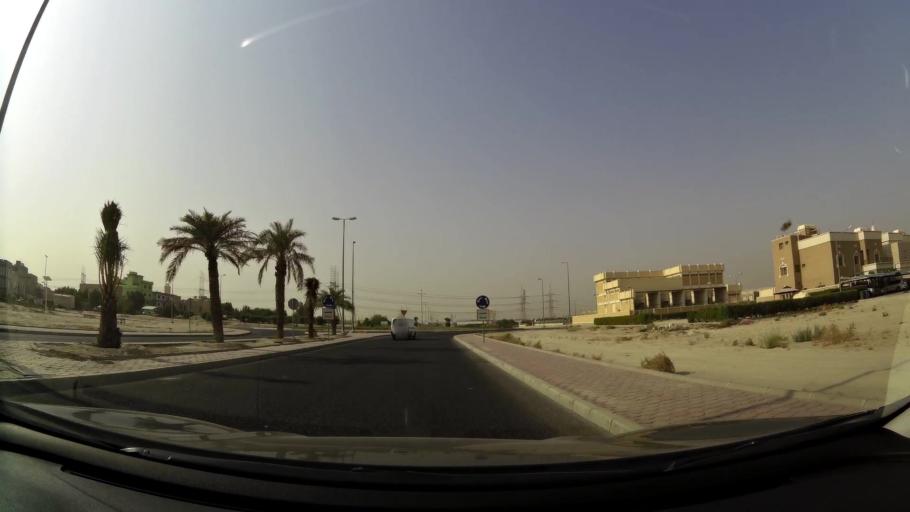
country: KW
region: Al Asimah
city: Ar Rabiyah
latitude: 29.2995
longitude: 47.8570
